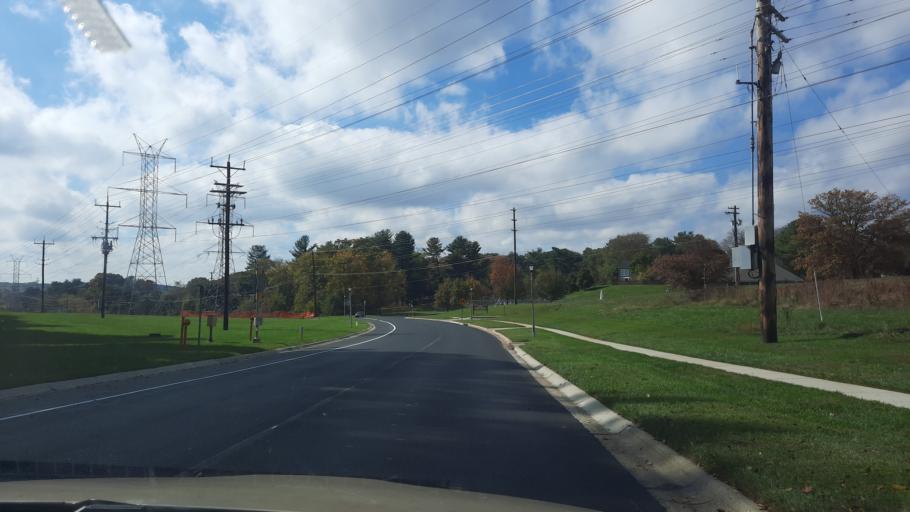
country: US
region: Maryland
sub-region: Montgomery County
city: Montgomery Village
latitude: 39.1712
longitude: -77.2117
